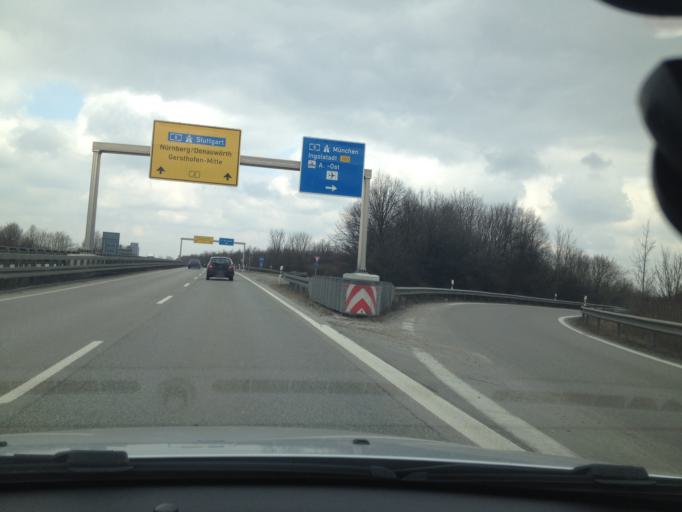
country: DE
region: Bavaria
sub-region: Swabia
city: Gersthofen
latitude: 48.4122
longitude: 10.8729
